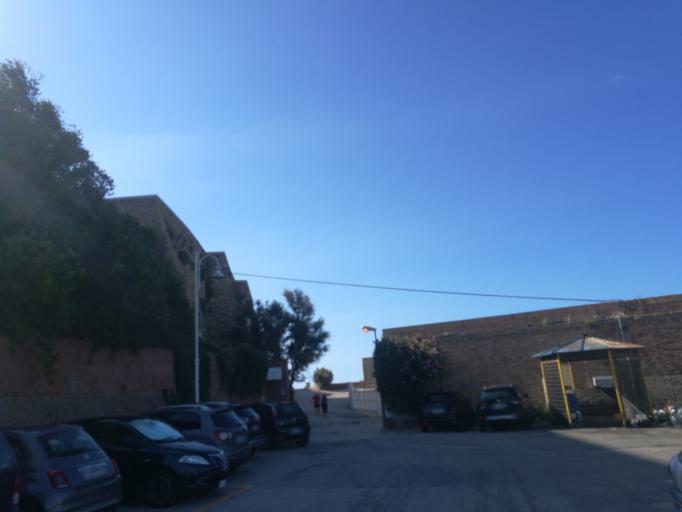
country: IT
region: Molise
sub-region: Provincia di Campobasso
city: Termoli
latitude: 42.0052
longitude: 14.9985
